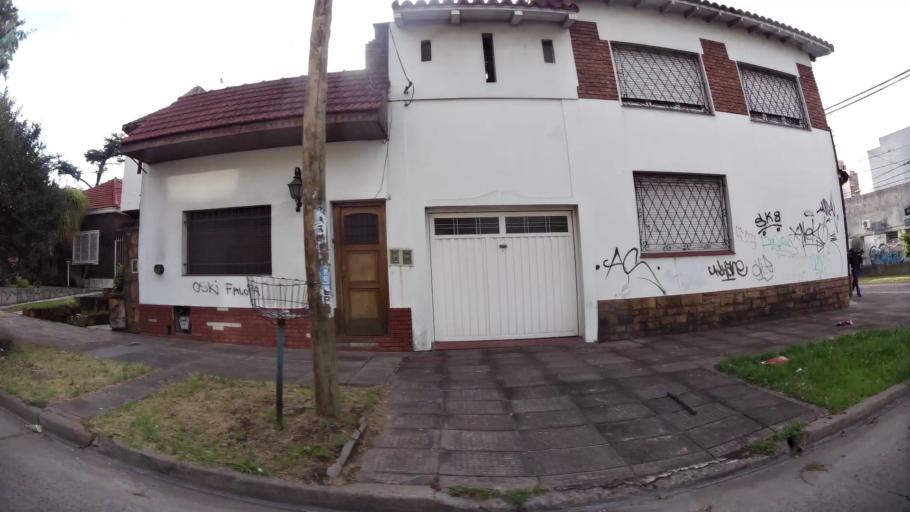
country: AR
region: Buenos Aires
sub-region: Partido de Moron
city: Moron
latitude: -34.6585
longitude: -58.6187
